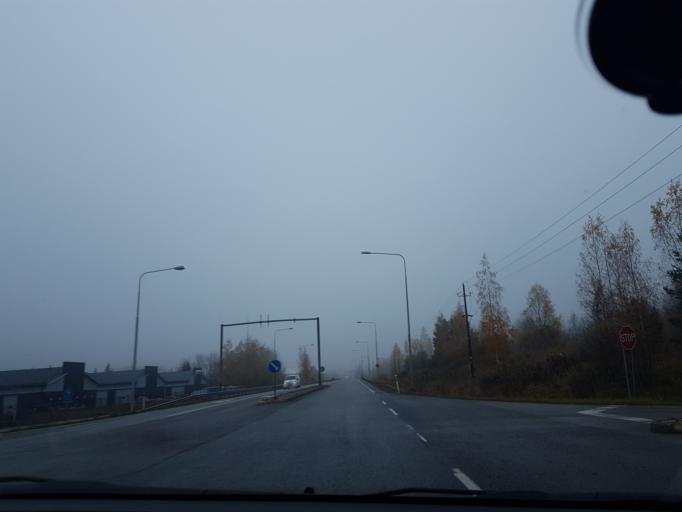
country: FI
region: Uusimaa
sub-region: Helsinki
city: Jaervenpaeae
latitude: 60.4630
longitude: 25.1395
